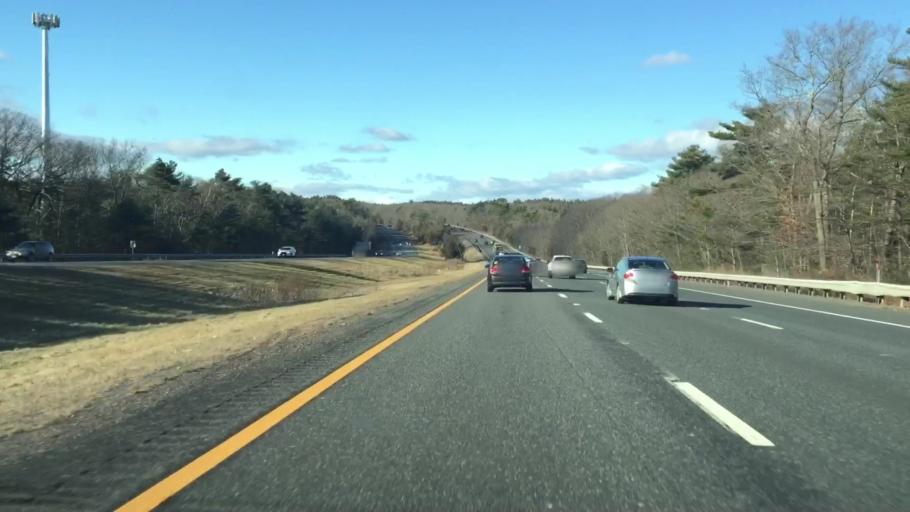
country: US
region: Massachusetts
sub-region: Norfolk County
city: Wrentham
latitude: 42.0489
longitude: -71.3642
